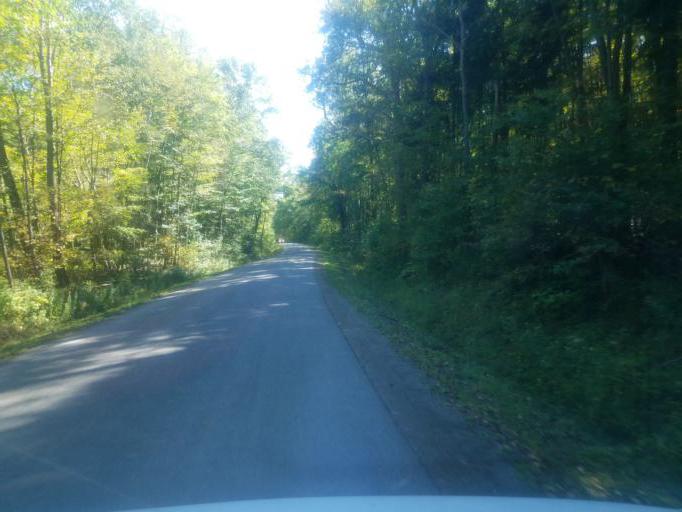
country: US
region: New York
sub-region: Allegany County
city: Cuba
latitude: 42.3121
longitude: -78.2049
